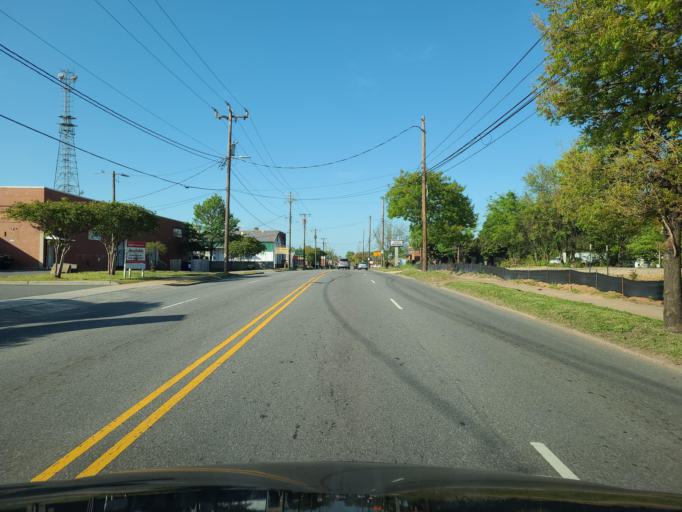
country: US
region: North Carolina
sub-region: Mecklenburg County
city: Charlotte
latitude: 35.2489
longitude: -80.8288
